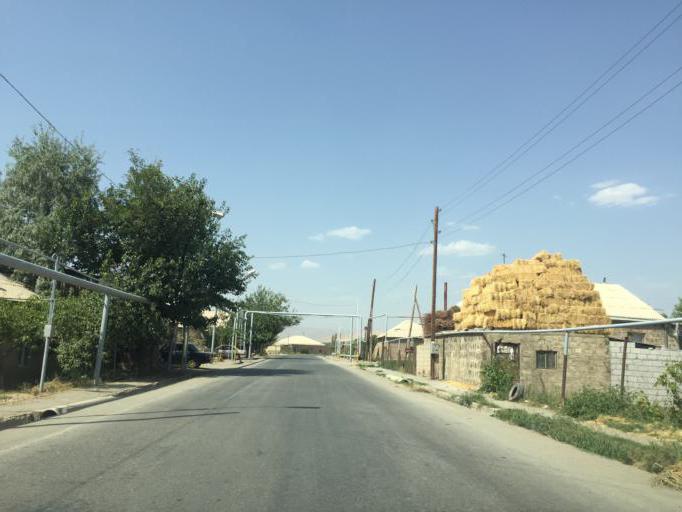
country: AM
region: Ararat
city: Shahumyan
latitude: 39.8982
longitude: 44.5979
